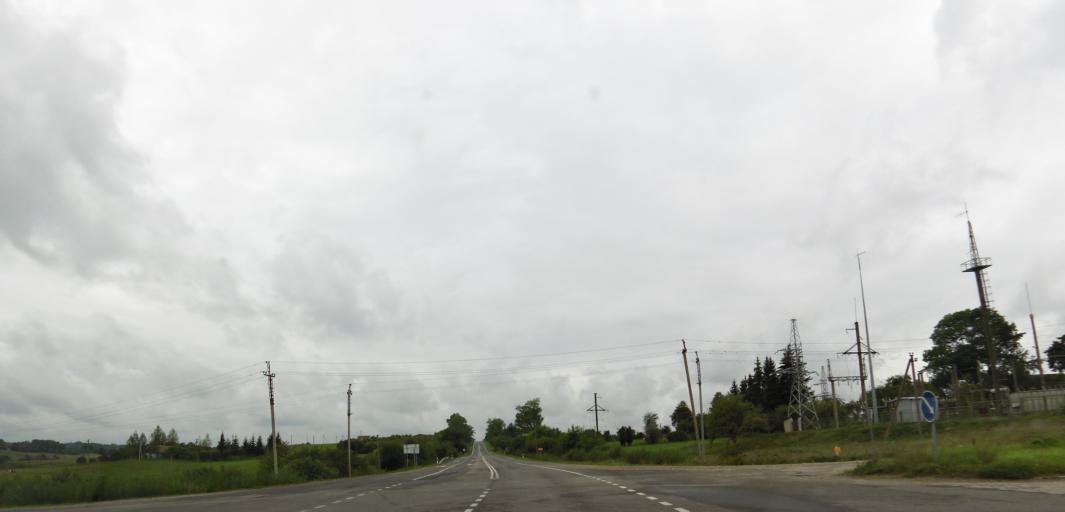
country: LT
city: Sirvintos
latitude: 55.2234
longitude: 25.0938
